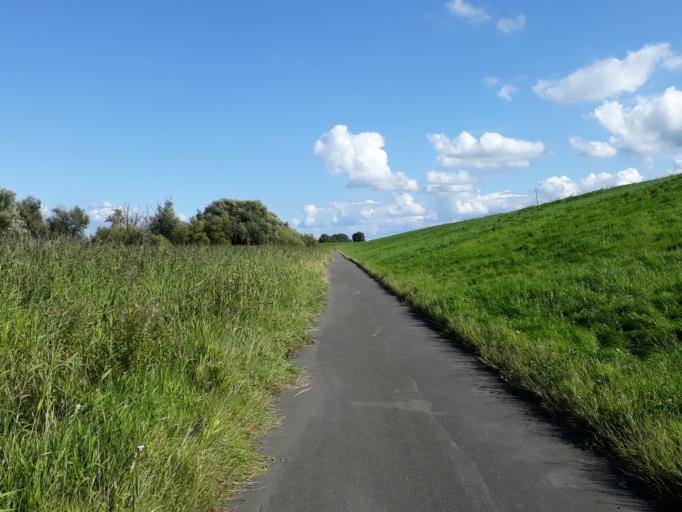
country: DE
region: Lower Saxony
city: Jork
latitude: 53.5494
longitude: 9.6783
